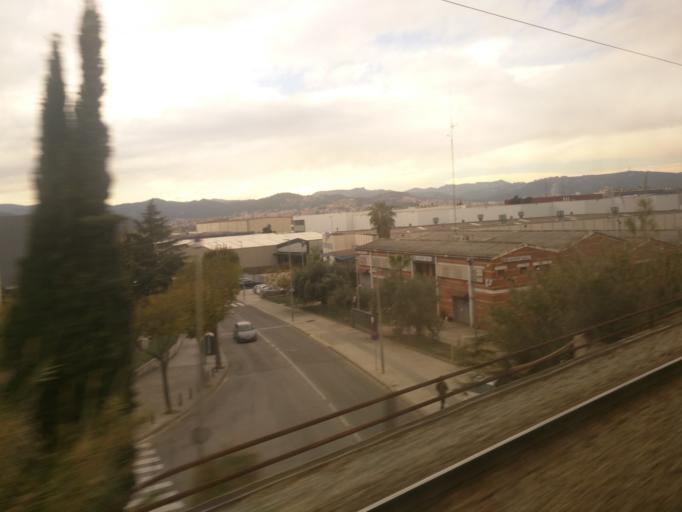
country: ES
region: Catalonia
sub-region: Provincia de Barcelona
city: Sant Feliu de Llobregat
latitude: 41.3882
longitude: 2.0421
